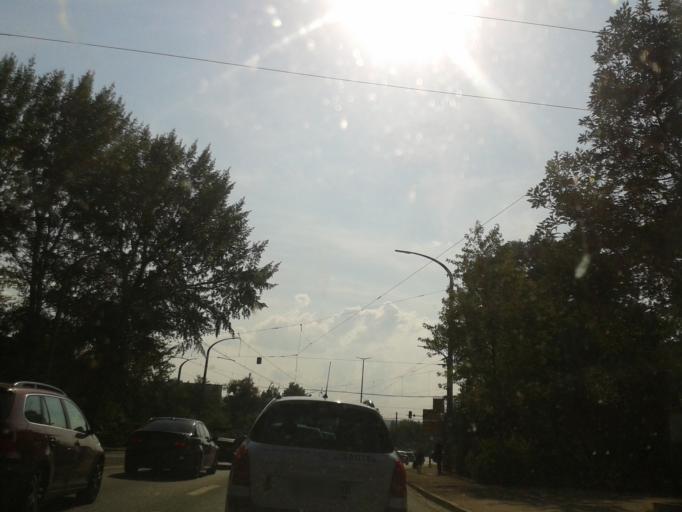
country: DE
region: Saxony
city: Dresden
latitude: 51.0392
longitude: 13.7478
